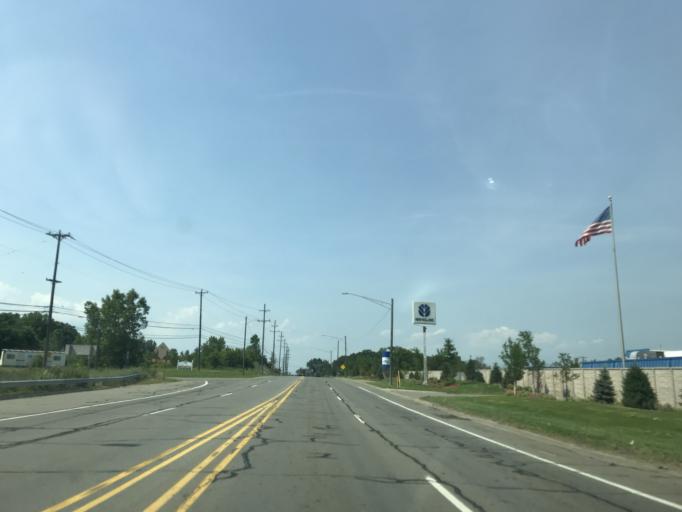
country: US
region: Michigan
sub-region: Wayne County
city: Woodhaven
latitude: 42.1853
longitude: -83.2673
